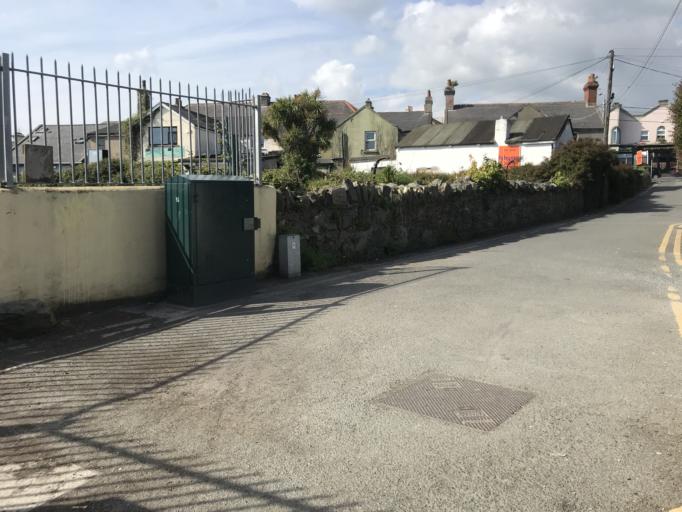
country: IE
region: Leinster
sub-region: Wicklow
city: Greystones
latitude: 53.1450
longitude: -6.0617
